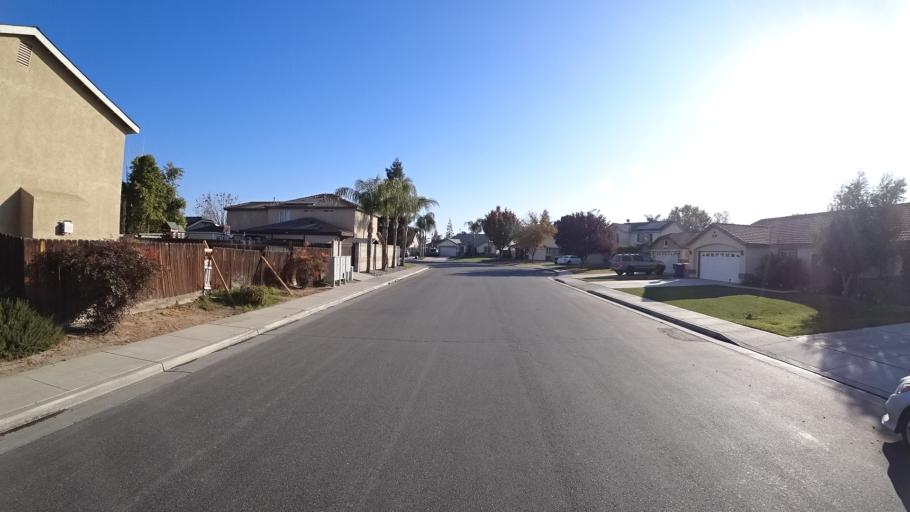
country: US
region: California
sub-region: Kern County
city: Greenfield
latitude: 35.2803
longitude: -119.0512
